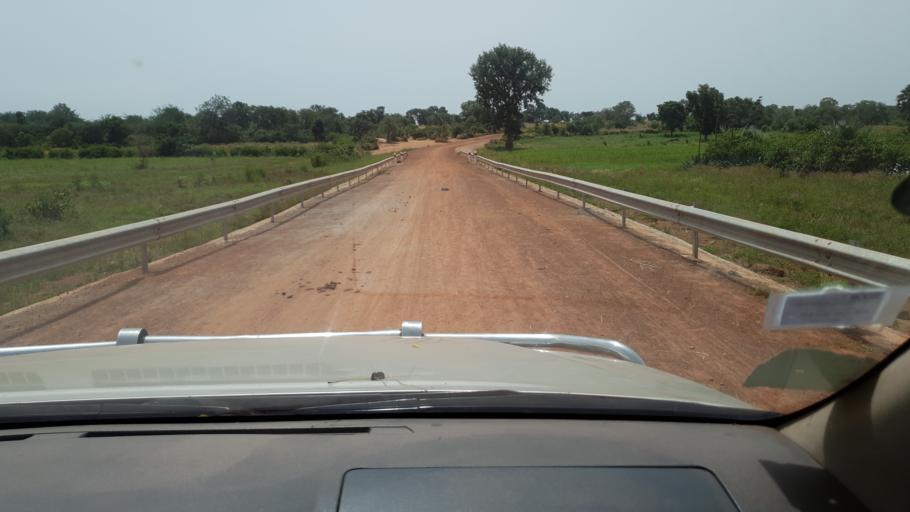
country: ML
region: Koulikoro
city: Kolokani
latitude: 13.4232
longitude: -8.2409
